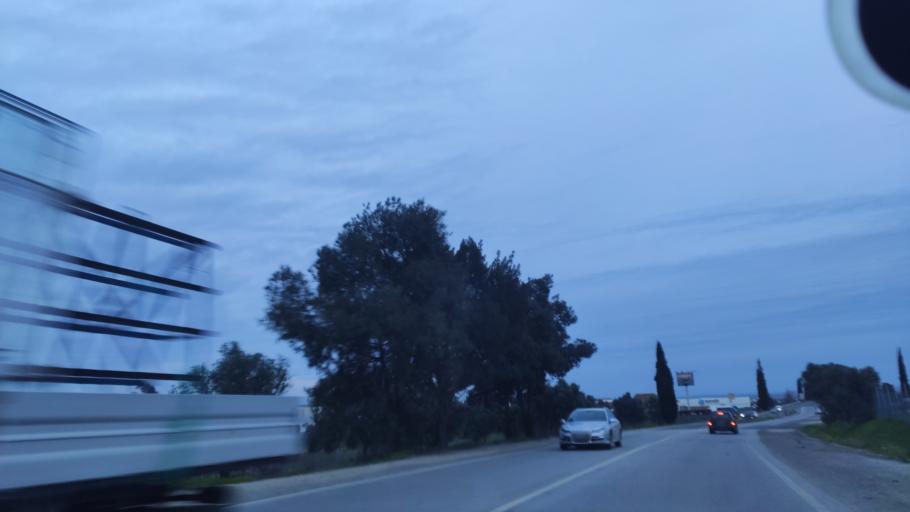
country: PT
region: Beja
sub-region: Beja
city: Beja
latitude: 38.0262
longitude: -7.8640
